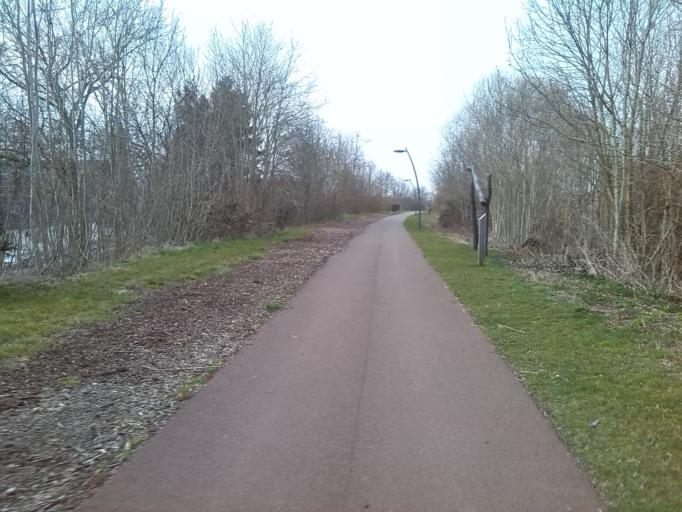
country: BE
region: Flanders
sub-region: Provincie West-Vlaanderen
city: Brugge
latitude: 51.2285
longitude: 3.2076
